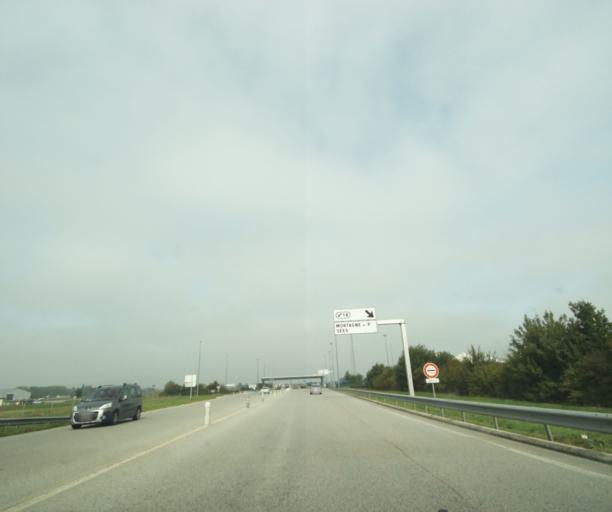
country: FR
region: Lower Normandy
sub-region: Departement de l'Orne
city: Sees
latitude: 48.6314
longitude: 0.1932
